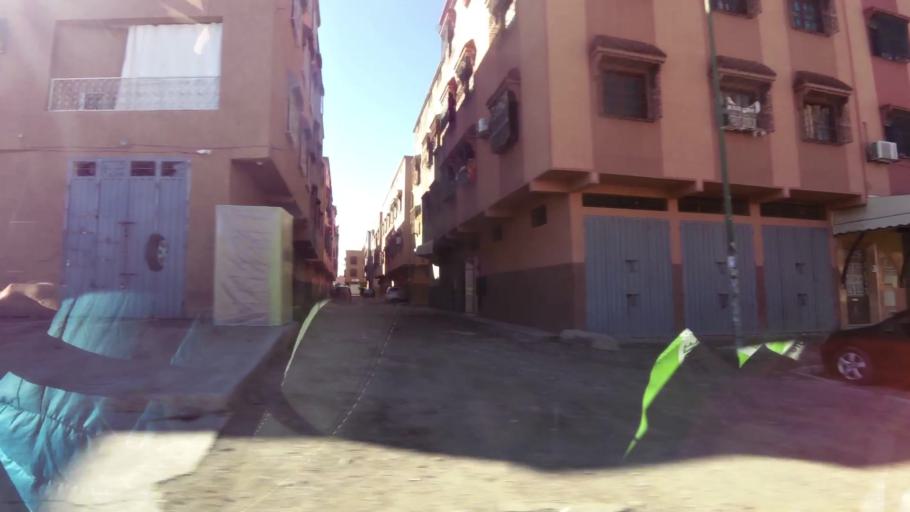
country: MA
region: Marrakech-Tensift-Al Haouz
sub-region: Marrakech
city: Marrakesh
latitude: 31.5976
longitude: -8.0397
